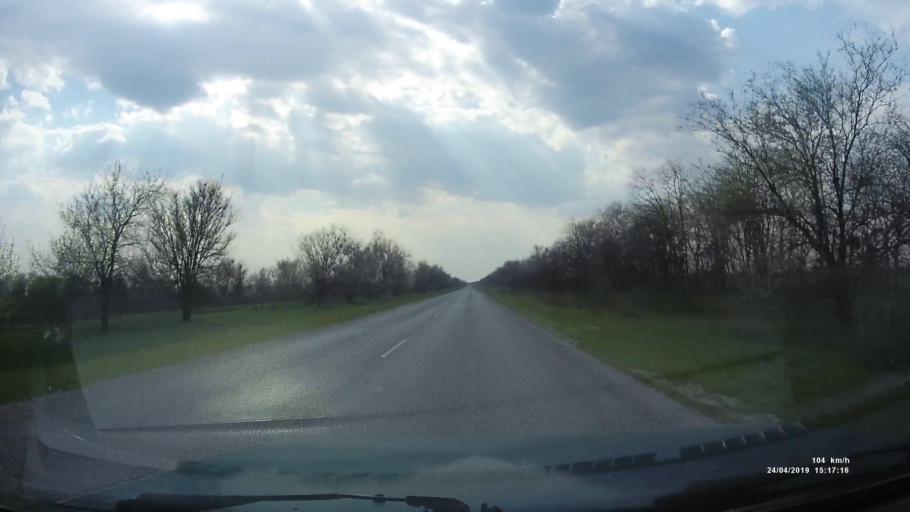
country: RU
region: Rostov
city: Remontnoye
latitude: 46.5465
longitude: 43.1937
